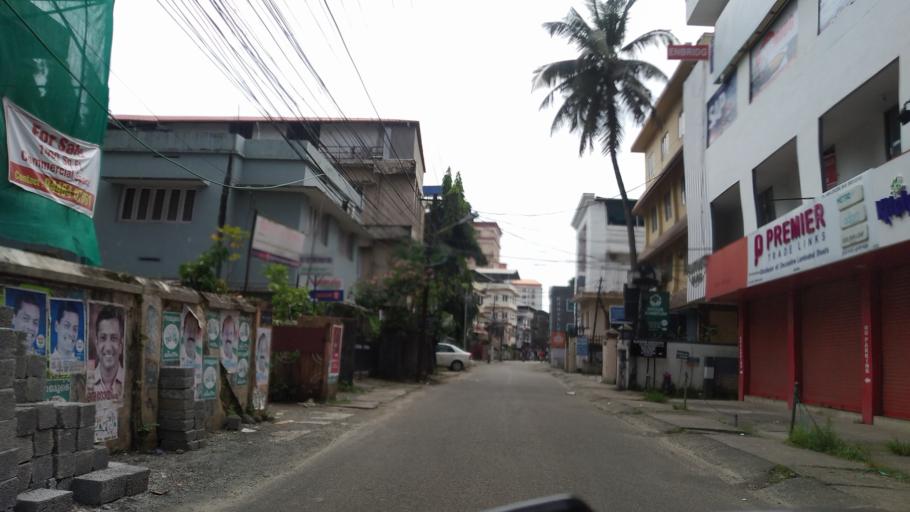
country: IN
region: Kerala
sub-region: Ernakulam
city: Cochin
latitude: 9.9735
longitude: 76.2827
